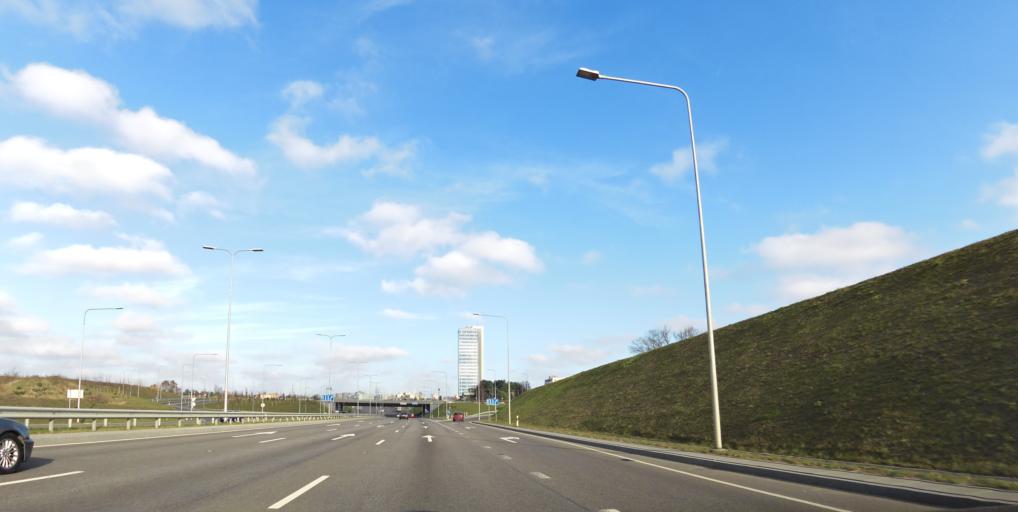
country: LT
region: Vilnius County
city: Justiniskes
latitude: 54.6979
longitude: 25.2070
